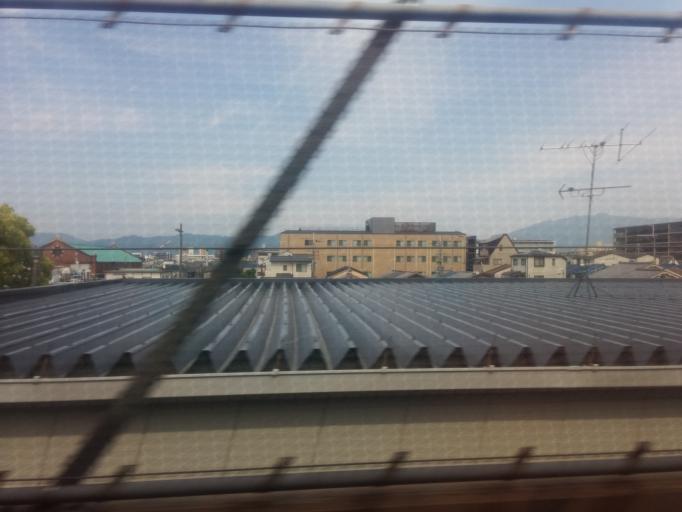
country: JP
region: Kyoto
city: Kyoto
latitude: 35.0063
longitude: 135.7417
